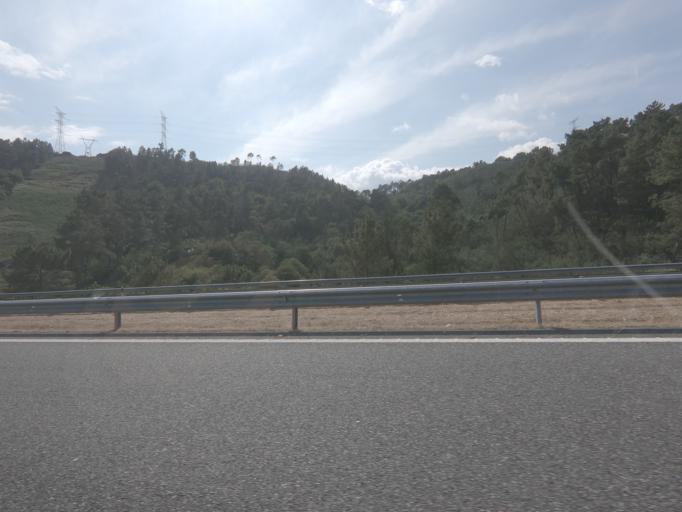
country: ES
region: Galicia
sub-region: Provincia de Ourense
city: Cenlle
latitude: 42.3272
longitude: -8.0767
